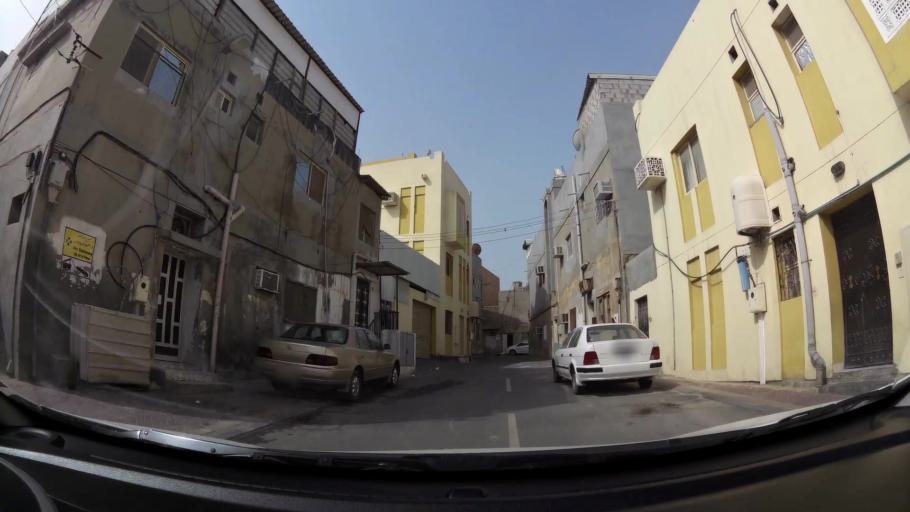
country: BH
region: Manama
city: Jidd Hafs
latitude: 26.2311
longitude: 50.5278
